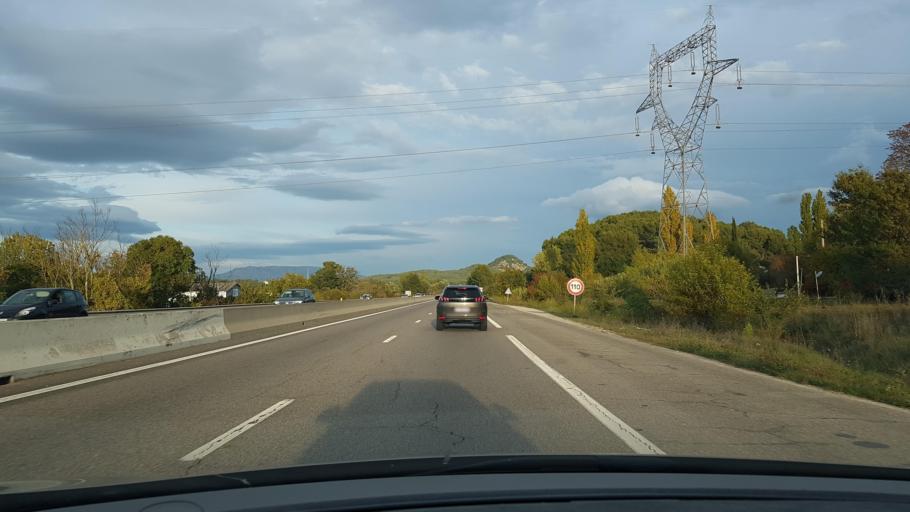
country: FR
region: Provence-Alpes-Cote d'Azur
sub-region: Departement des Bouches-du-Rhone
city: Bouc-Bel-Air
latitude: 43.4288
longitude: 5.4075
